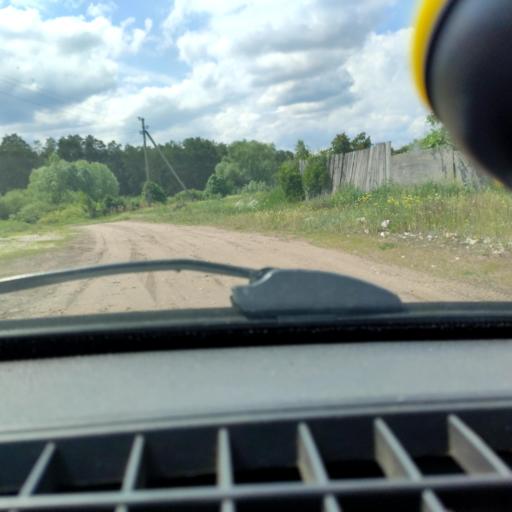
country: RU
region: Samara
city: Povolzhskiy
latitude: 53.6322
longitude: 49.6748
